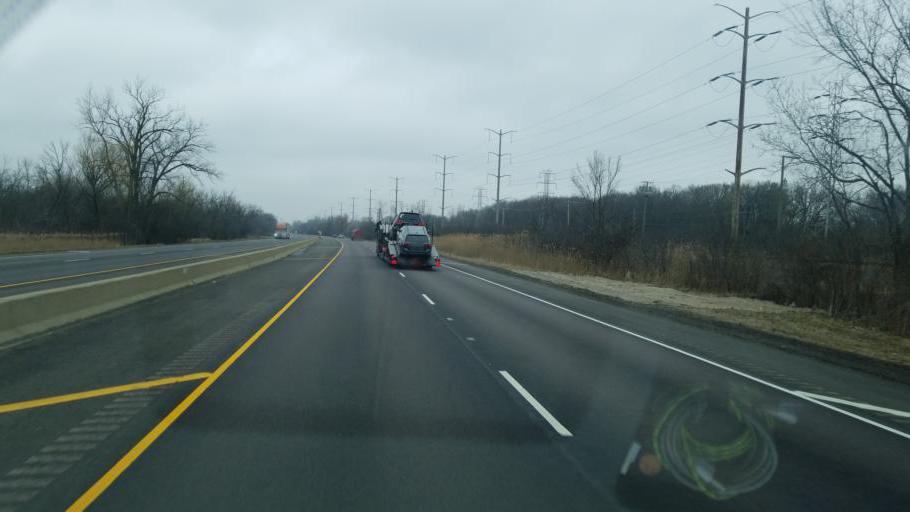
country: US
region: Illinois
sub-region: Lake County
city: Lake Forest
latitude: 42.2612
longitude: -87.8625
